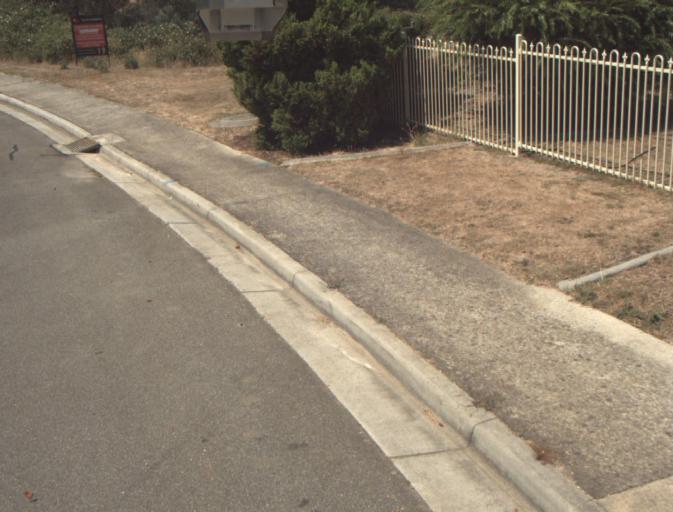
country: AU
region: Tasmania
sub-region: Launceston
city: Newstead
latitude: -41.4697
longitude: 147.1835
